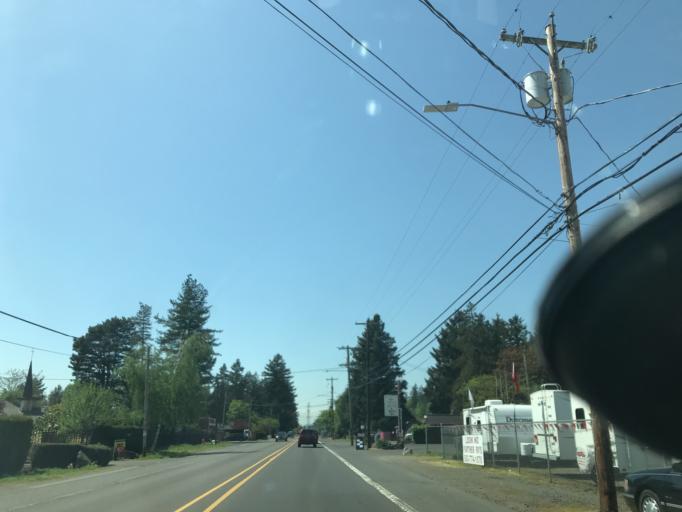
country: US
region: Oregon
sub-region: Multnomah County
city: Lents
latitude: 45.4964
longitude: -122.5504
